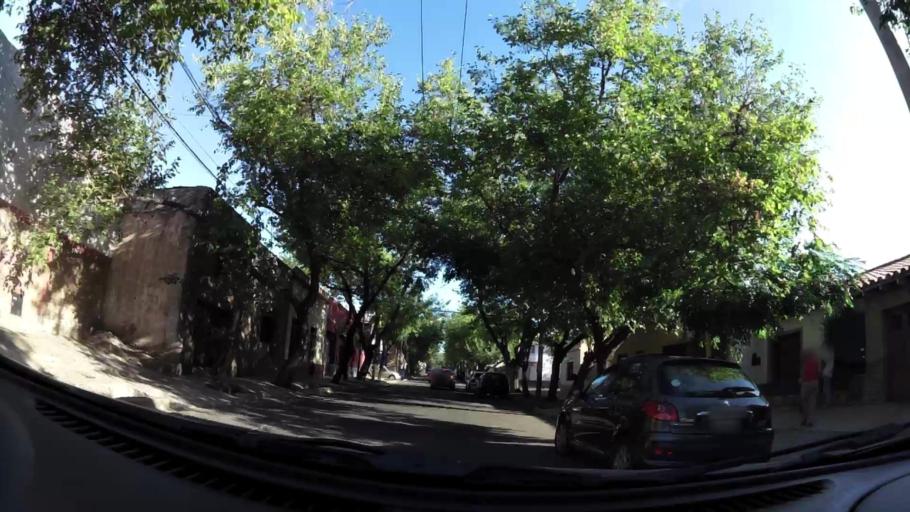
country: AR
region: Mendoza
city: Mendoza
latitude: -32.9023
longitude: -68.8288
